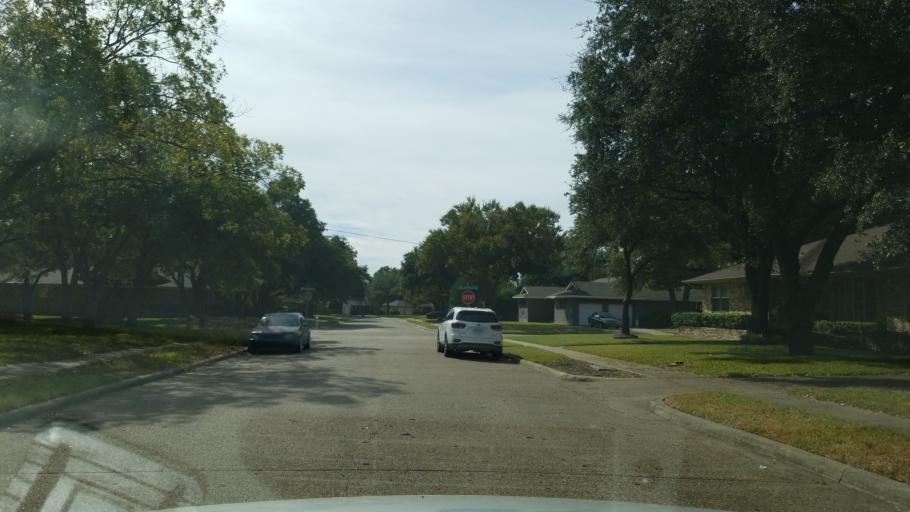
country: US
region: Texas
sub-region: Dallas County
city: Garland
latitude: 32.9024
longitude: -96.6629
